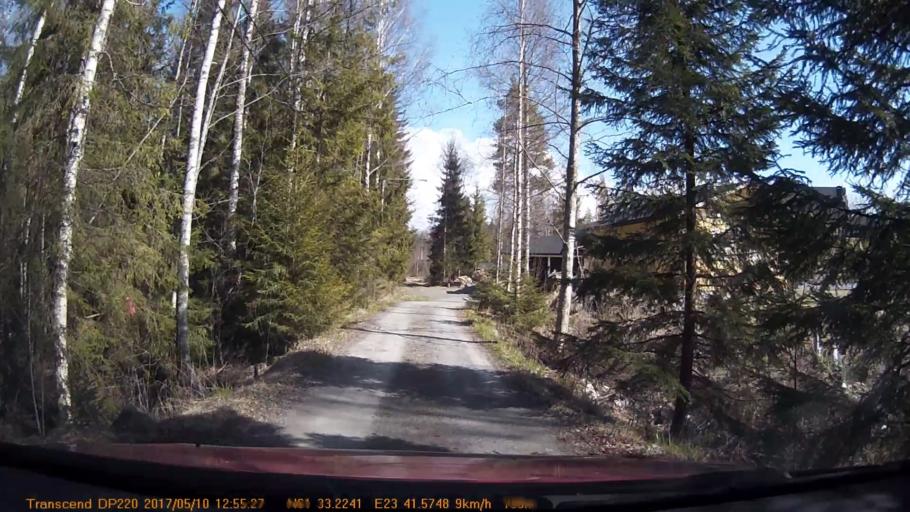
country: FI
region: Pirkanmaa
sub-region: Tampere
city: Yloejaervi
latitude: 61.5537
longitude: 23.6929
